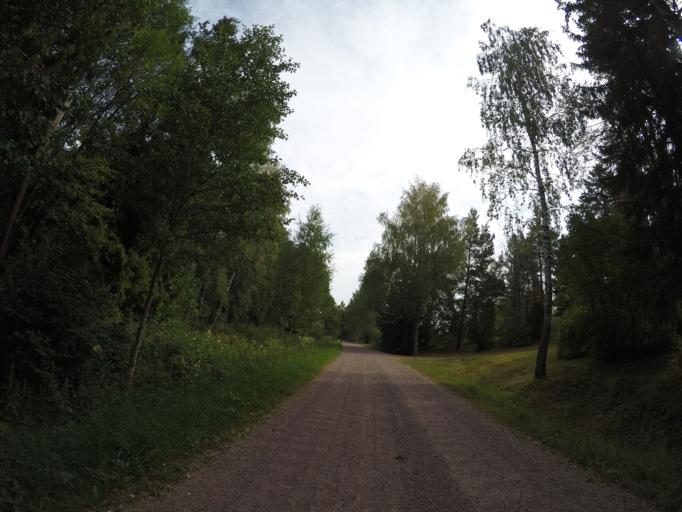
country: AX
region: Alands landsbygd
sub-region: Finstroem
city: Finstroem
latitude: 60.2264
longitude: 19.8483
